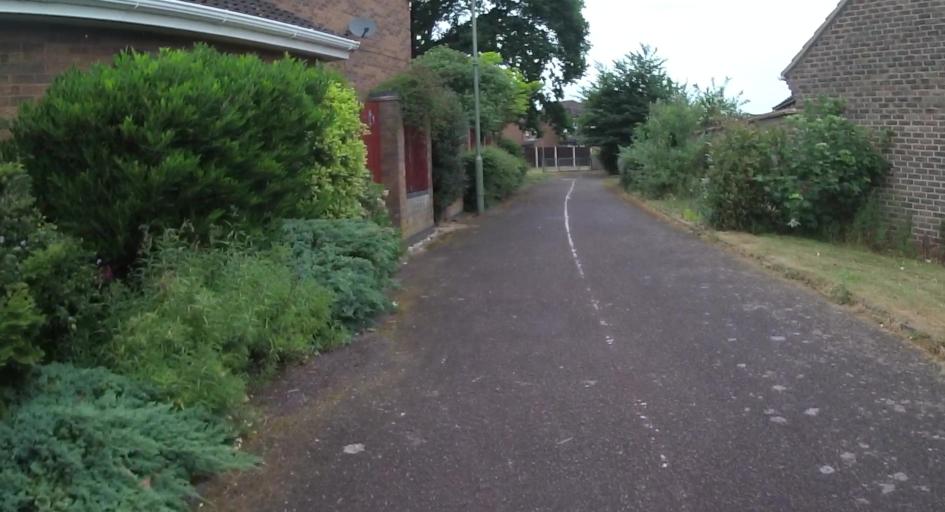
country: GB
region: England
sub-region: Hampshire
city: Farnborough
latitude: 51.2897
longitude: -0.7902
